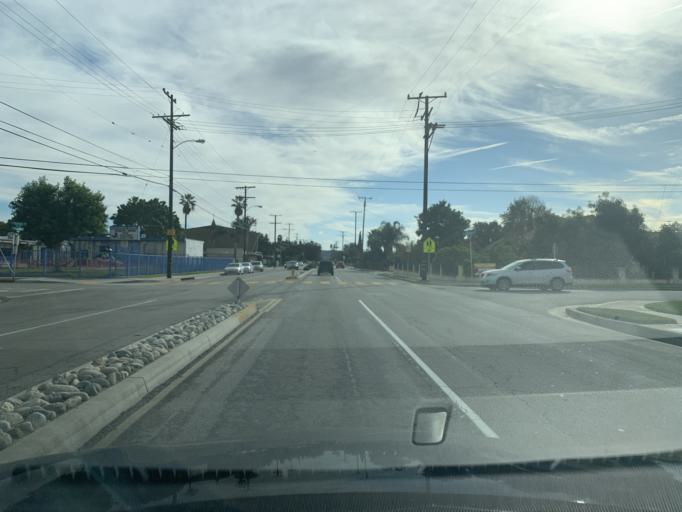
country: US
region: California
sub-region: Los Angeles County
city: South El Monte
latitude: 34.0576
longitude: -118.0424
